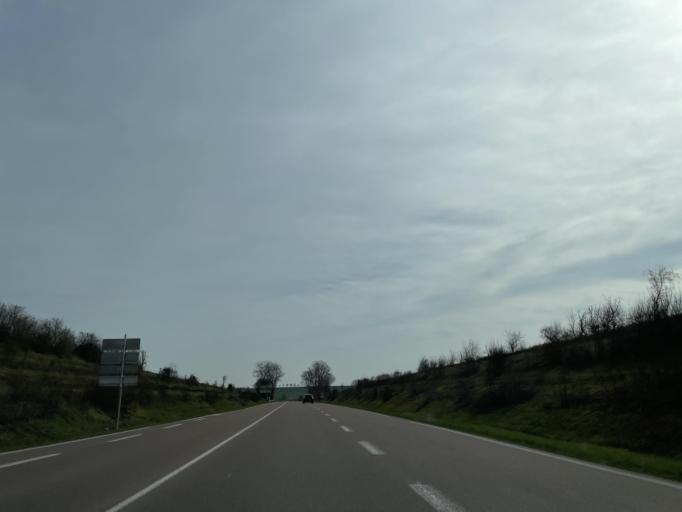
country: FR
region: Champagne-Ardenne
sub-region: Departement de l'Aube
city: Nogent-sur-Seine
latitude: 48.4828
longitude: 3.4916
